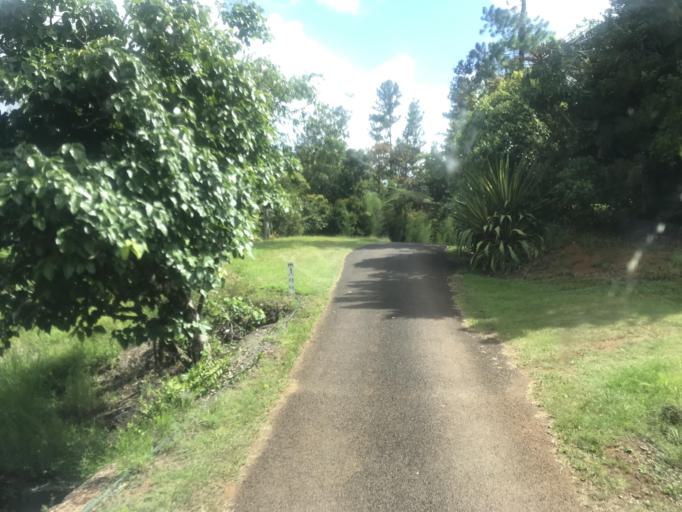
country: AU
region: Queensland
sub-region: Tablelands
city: Ravenshoe
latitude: -17.5506
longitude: 145.6976
